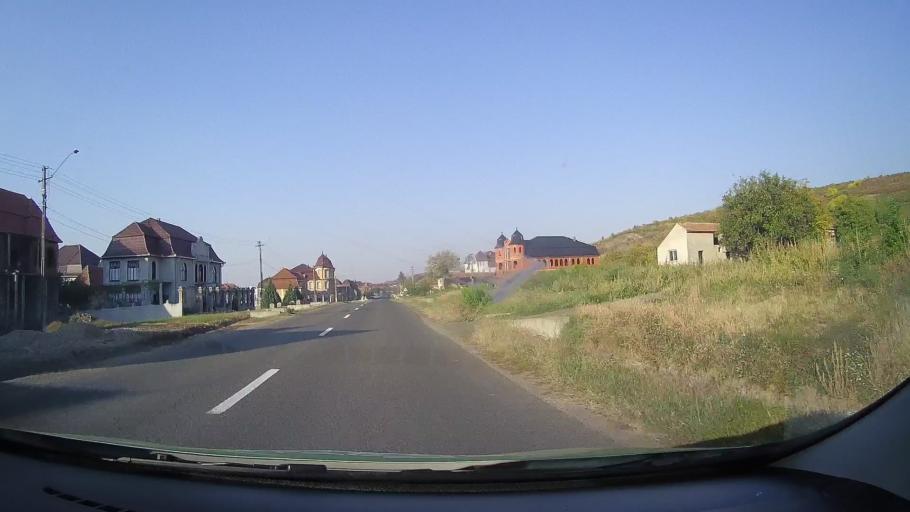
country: RO
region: Arad
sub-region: Comuna Covasint
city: Covasint
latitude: 46.1916
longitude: 21.6054
